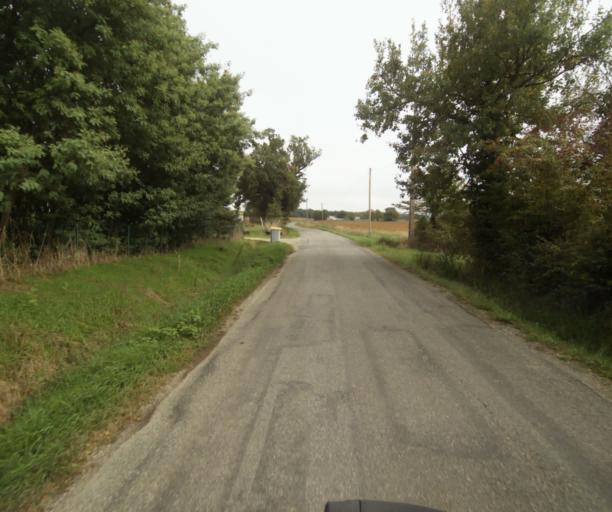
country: FR
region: Midi-Pyrenees
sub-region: Departement du Tarn-et-Garonne
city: Orgueil
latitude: 43.8898
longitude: 1.3843
